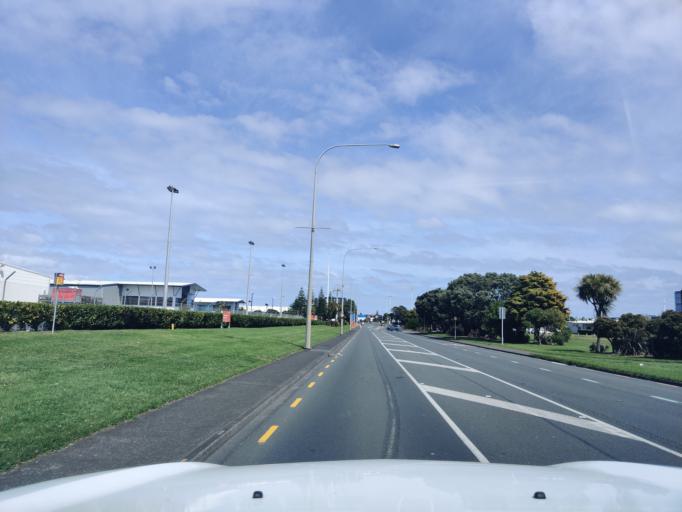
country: NZ
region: Auckland
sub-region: Auckland
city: Mangere
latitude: -37.0007
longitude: 174.7932
